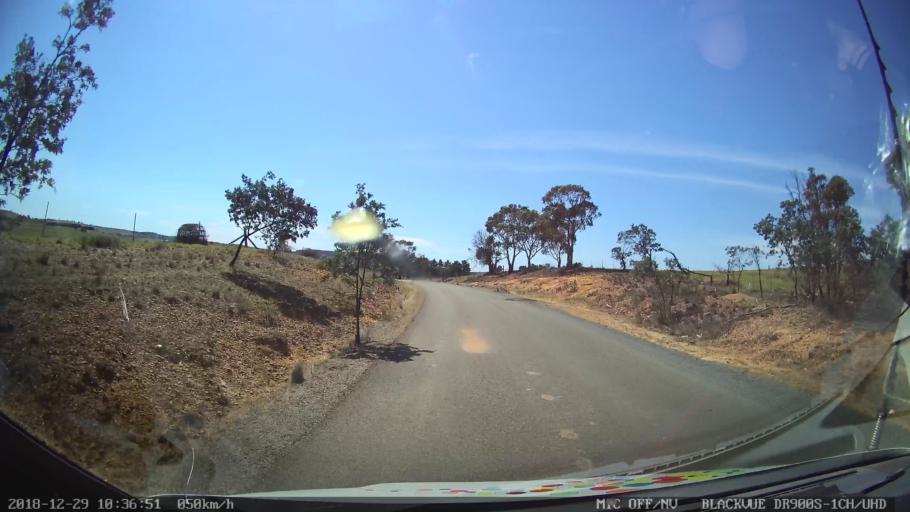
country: AU
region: New South Wales
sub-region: Yass Valley
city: Gundaroo
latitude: -34.9959
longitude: 149.4937
